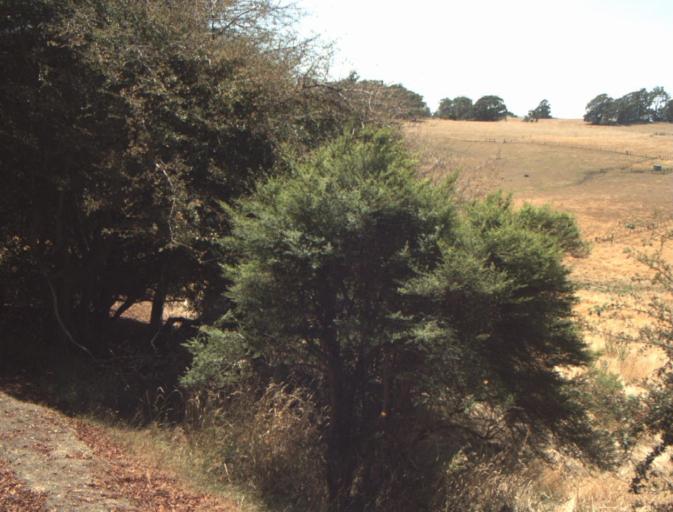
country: AU
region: Tasmania
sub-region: Launceston
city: Mayfield
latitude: -41.2485
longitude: 147.1209
